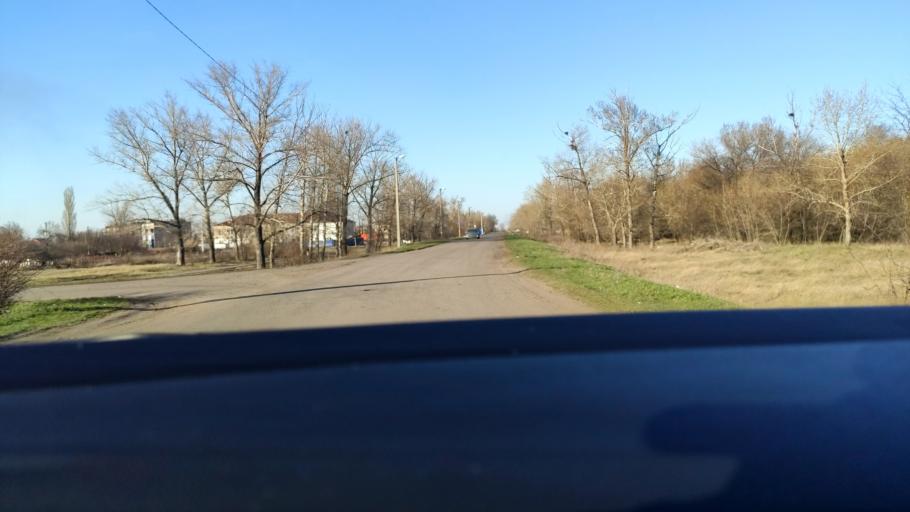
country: RU
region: Voronezj
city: Maslovka
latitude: 51.5093
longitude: 39.2940
